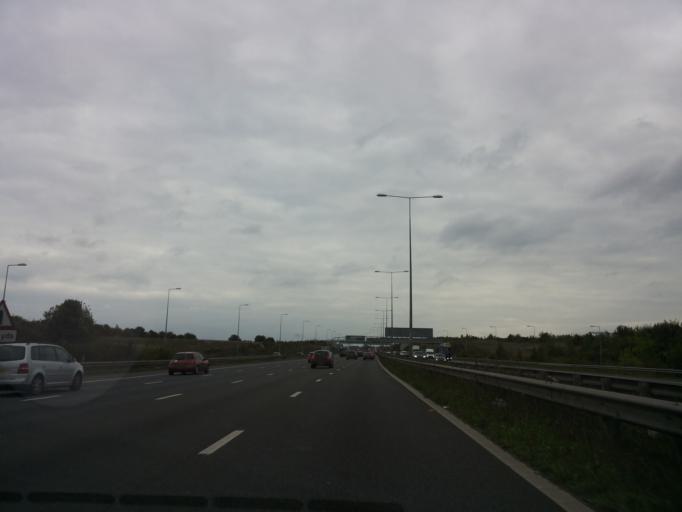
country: GB
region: England
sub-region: Kent
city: Gravesend
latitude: 51.4157
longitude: 0.3598
